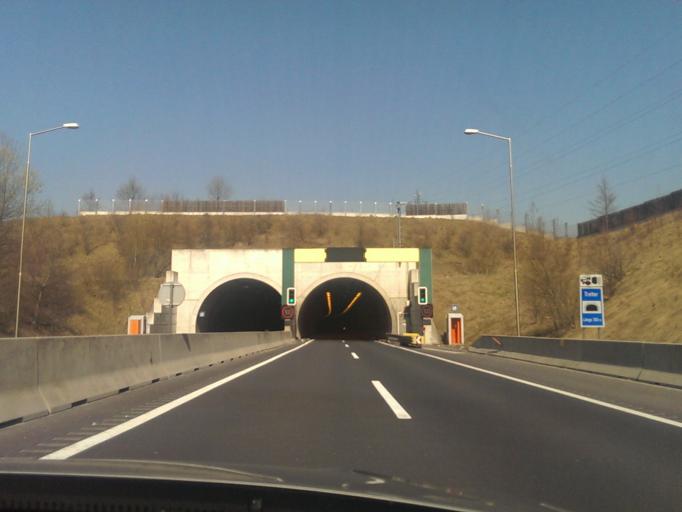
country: AT
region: Upper Austria
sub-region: Politischer Bezirk Kirchdorf an der Krems
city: Micheldorf in Oberoesterreich
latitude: 47.9190
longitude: 14.1017
